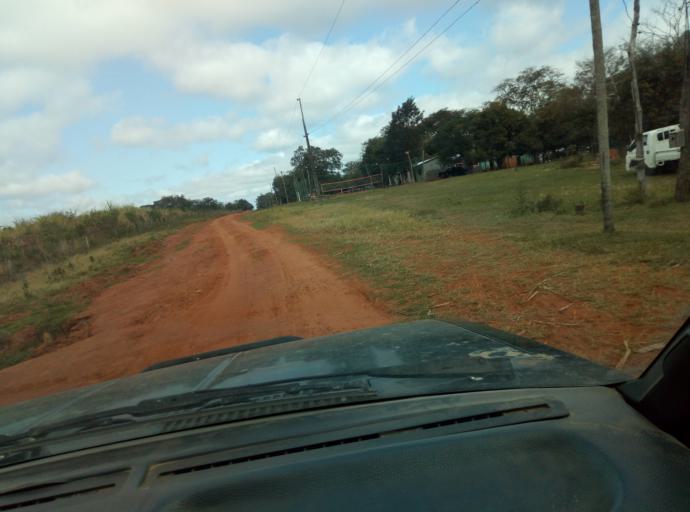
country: PY
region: Caaguazu
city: Doctor Cecilio Baez
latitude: -25.1504
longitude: -56.2909
